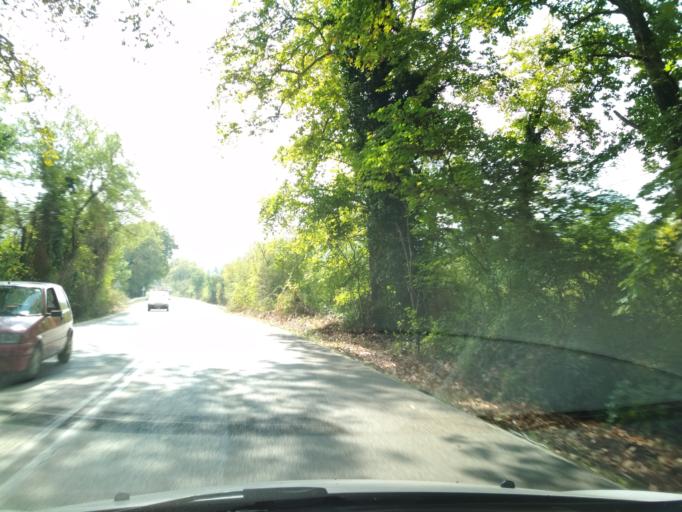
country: GR
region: Central Greece
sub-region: Nomos Evvoias
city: Prokopion
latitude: 38.7265
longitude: 23.5039
